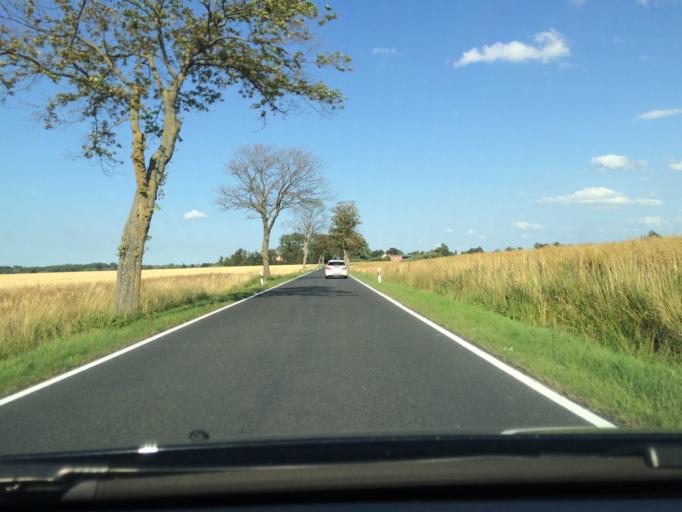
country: DE
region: Mecklenburg-Vorpommern
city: Niepars
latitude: 54.3349
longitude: 12.9191
